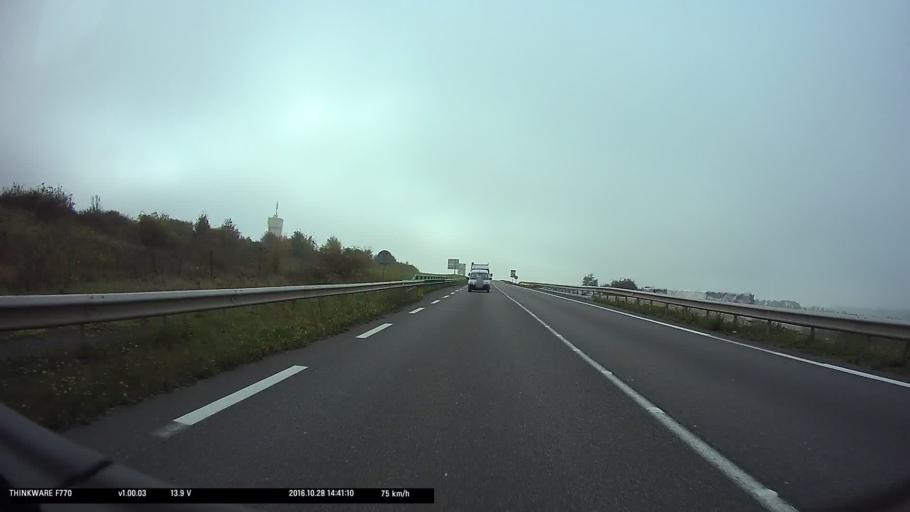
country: FR
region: Lorraine
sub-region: Departement de la Moselle
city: Lorquin
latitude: 48.6828
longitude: 6.9549
